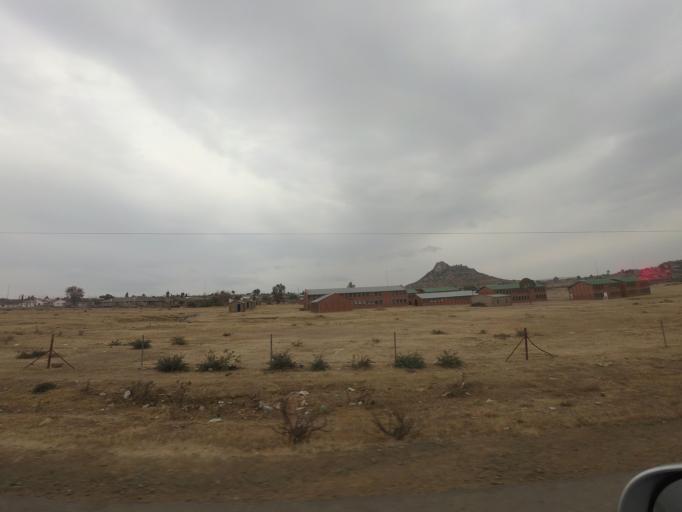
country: LS
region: Maseru
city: Maseru
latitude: -29.3530
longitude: 27.5467
